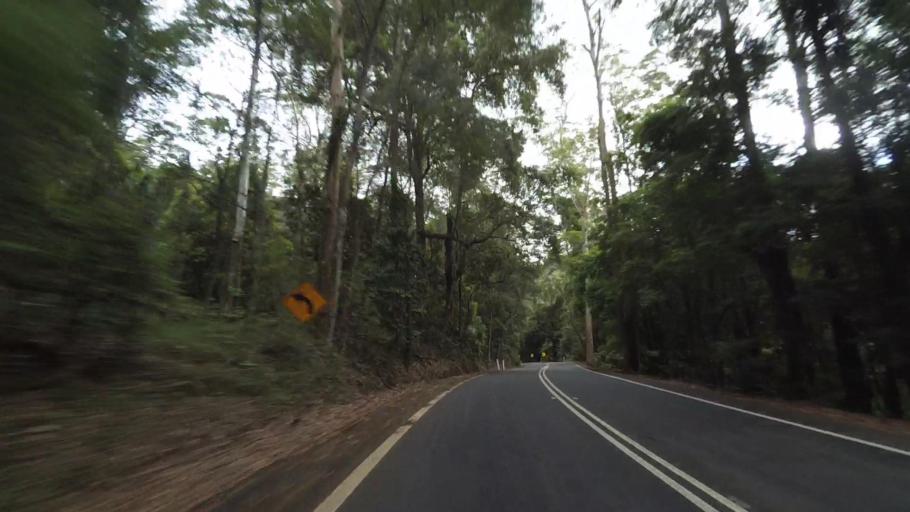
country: AU
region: New South Wales
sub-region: Wollongong
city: Helensburgh
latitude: -34.1675
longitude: 151.0168
